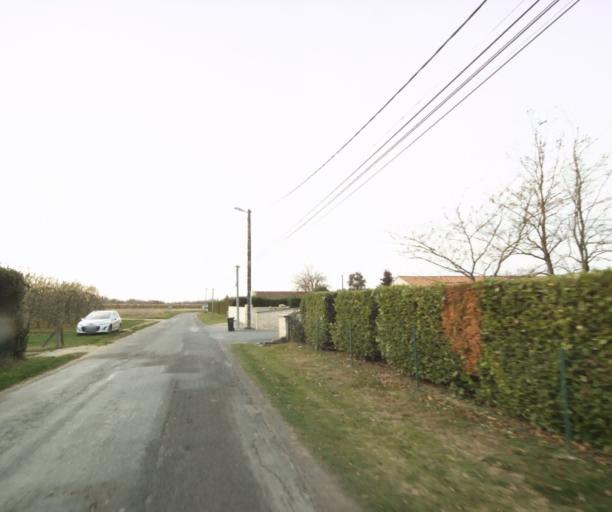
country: FR
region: Poitou-Charentes
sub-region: Departement de la Charente-Maritime
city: Fontcouverte
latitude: 45.7872
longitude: -0.5731
